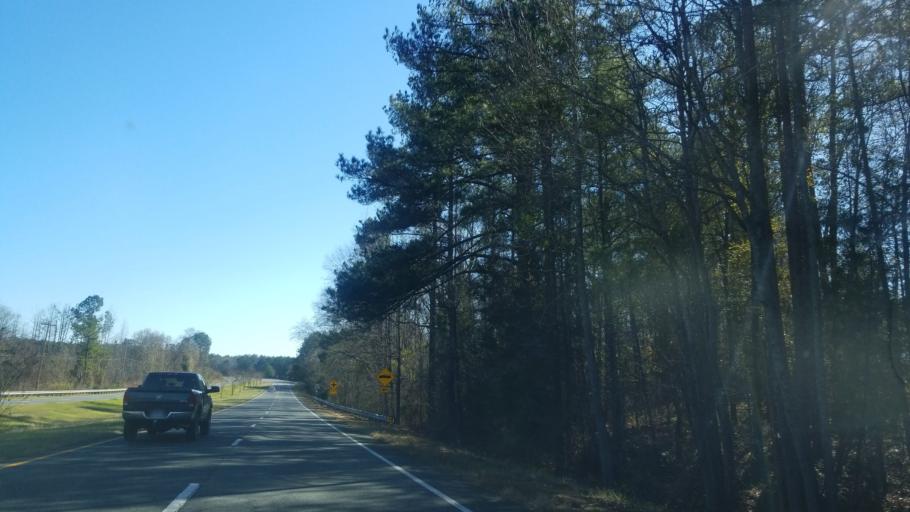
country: US
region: Georgia
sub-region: Talbot County
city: Talbotton
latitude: 32.5486
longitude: -84.7314
